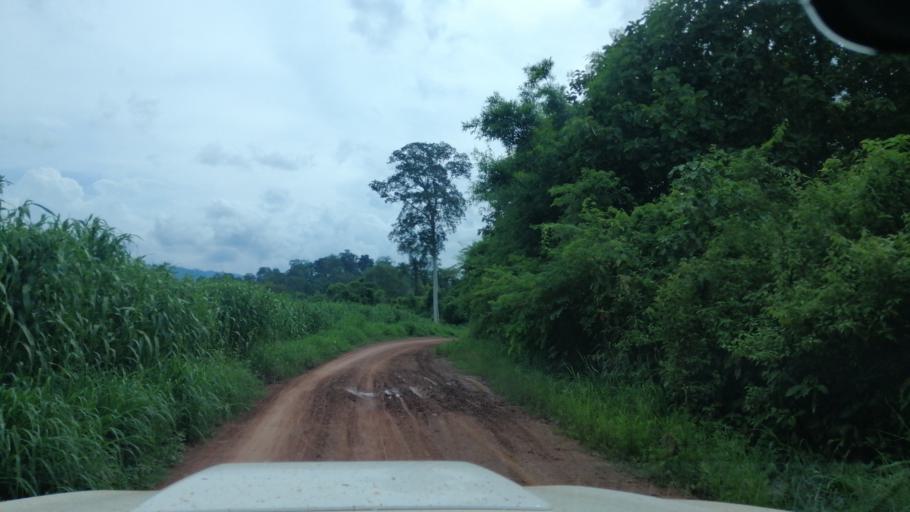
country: TH
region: Nan
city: Mae Charim
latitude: 18.7754
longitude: 101.3162
